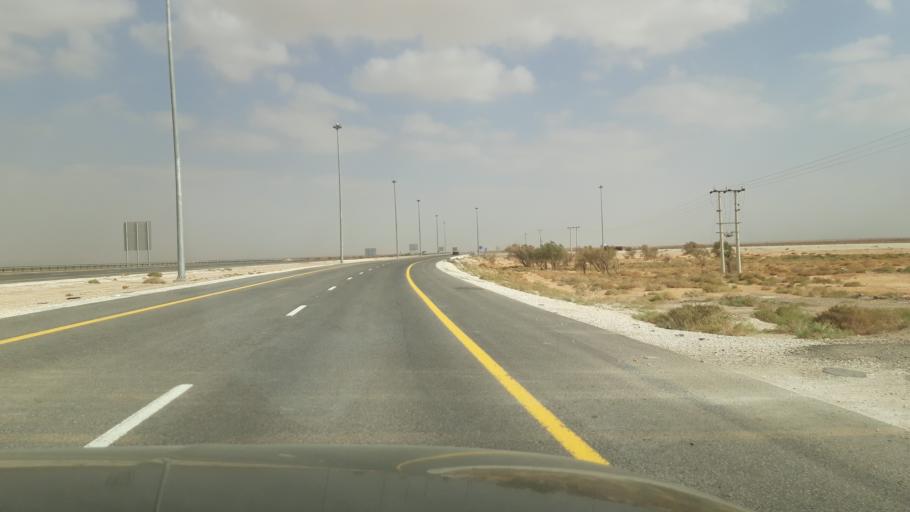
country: JO
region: Amman
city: Al Azraq ash Shamali
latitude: 31.7810
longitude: 36.7928
